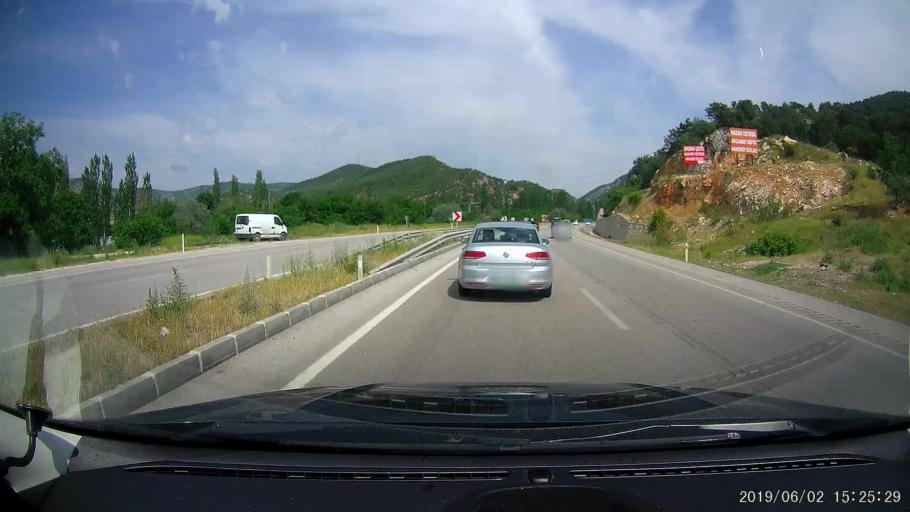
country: TR
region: Amasya
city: Saraycik
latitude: 40.9928
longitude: 35.0221
